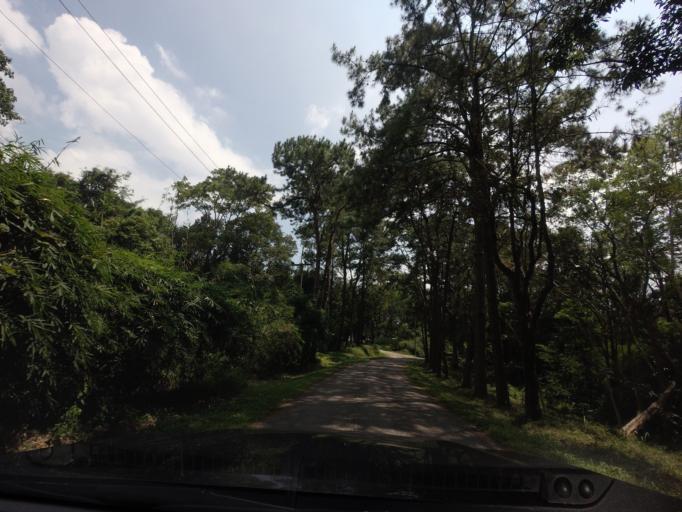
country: TH
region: Loei
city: Phu Ruea
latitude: 17.4804
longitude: 101.3523
